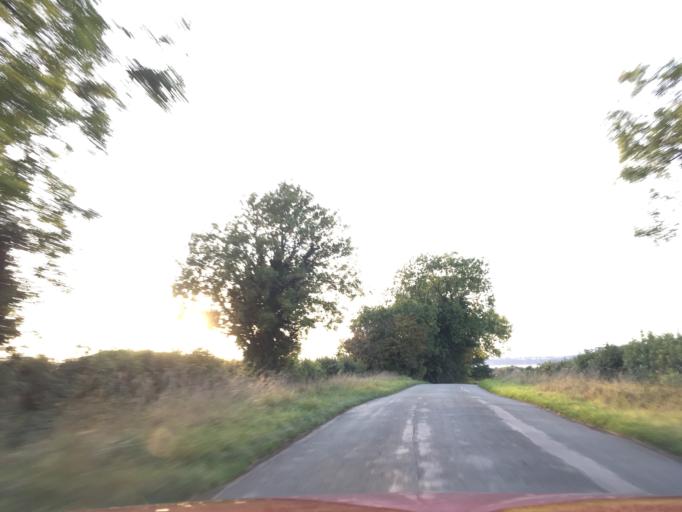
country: GB
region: England
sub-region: South Gloucestershire
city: Alveston
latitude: 51.6188
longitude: -2.5654
